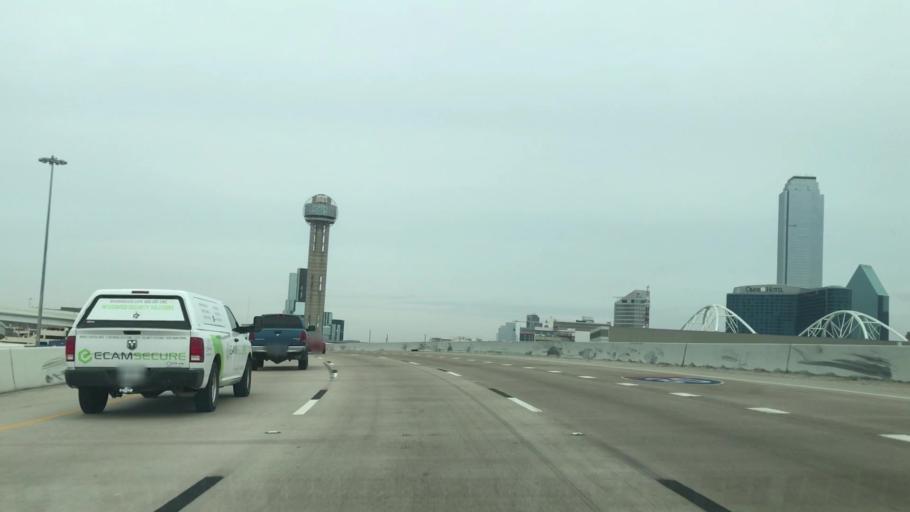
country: US
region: Texas
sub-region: Dallas County
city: Dallas
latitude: 32.7683
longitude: -96.8043
